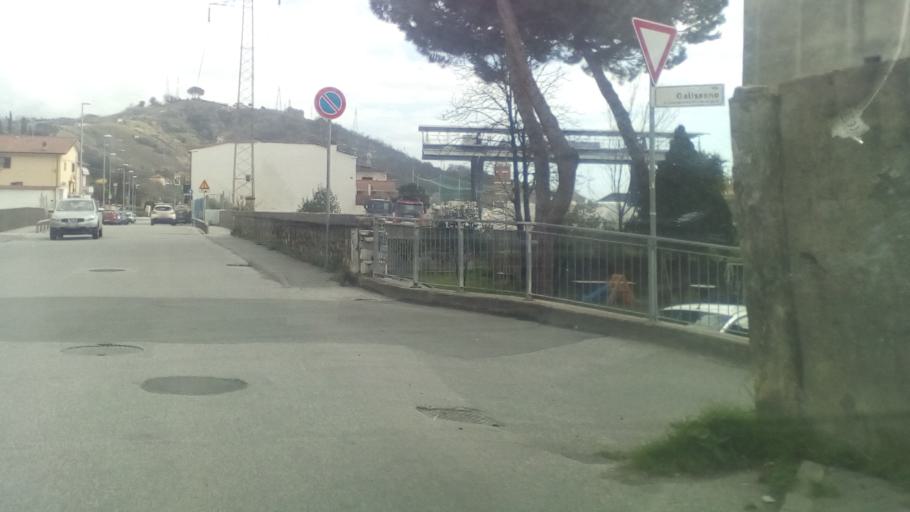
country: IT
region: Tuscany
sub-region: Provincia di Massa-Carrara
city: Carrara
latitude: 44.0575
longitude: 10.0727
